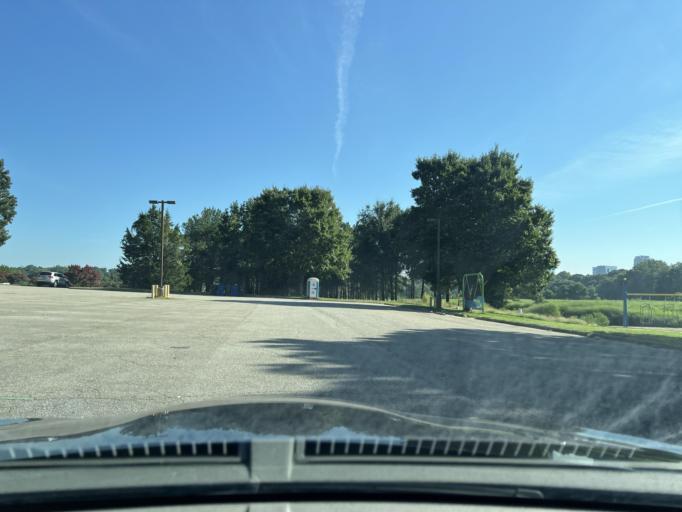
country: US
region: North Carolina
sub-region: Wake County
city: West Raleigh
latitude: 35.7714
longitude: -78.6617
